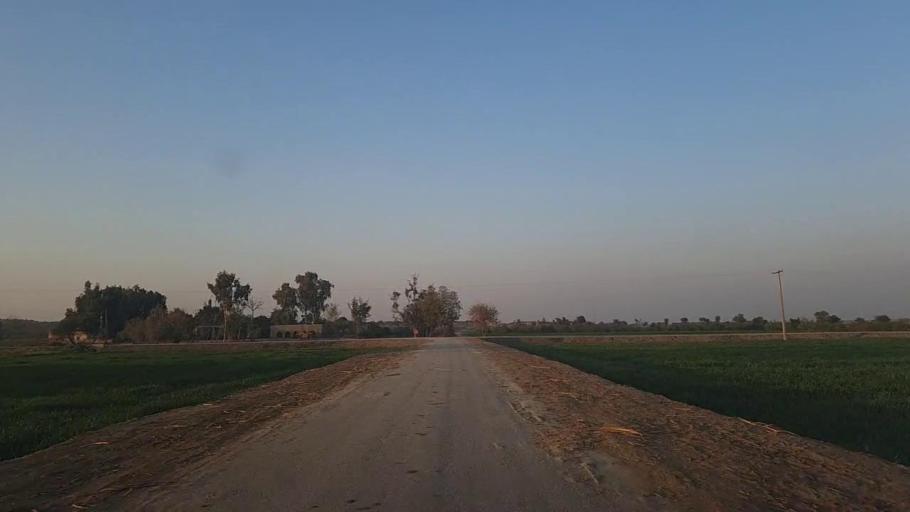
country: PK
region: Sindh
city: Jam Sahib
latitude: 26.3513
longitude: 68.7147
